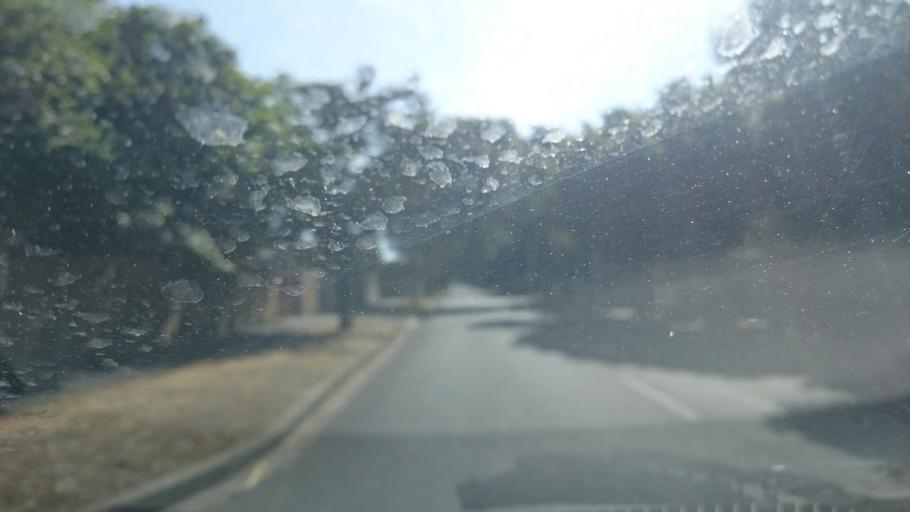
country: ZA
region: Western Cape
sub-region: City of Cape Town
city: Lansdowne
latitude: -34.0186
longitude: 18.4785
